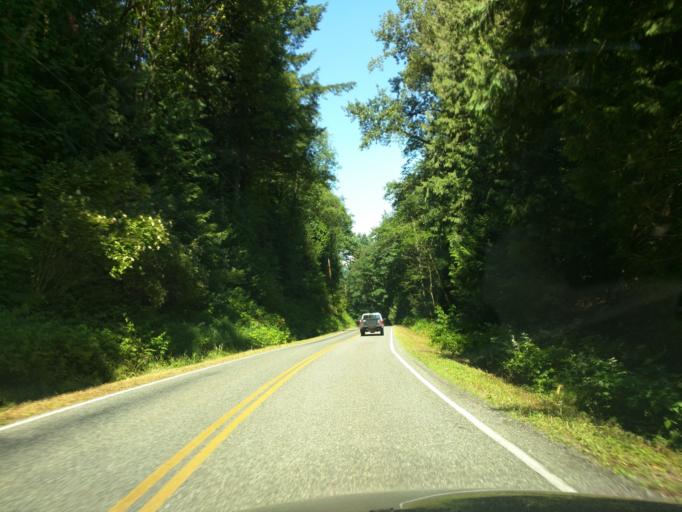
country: US
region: Washington
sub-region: Whatcom County
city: Peaceful Valley
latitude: 48.9640
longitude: -122.1703
